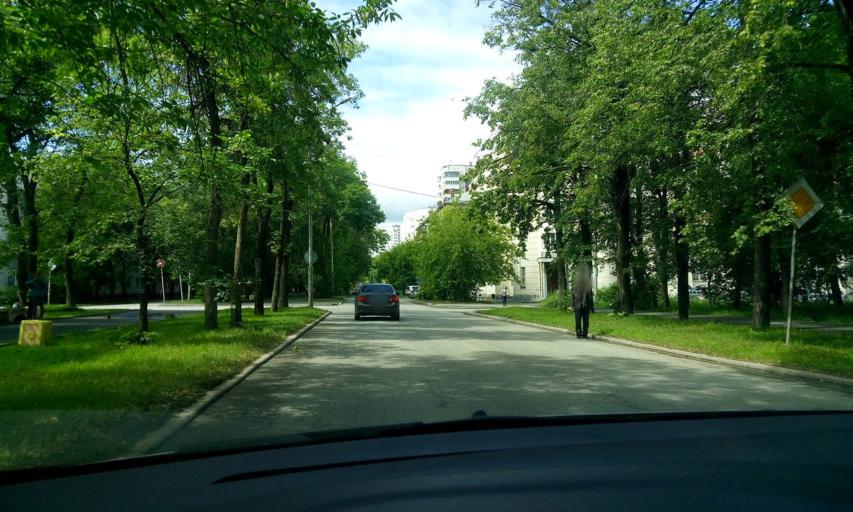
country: RU
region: Sverdlovsk
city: Yekaterinburg
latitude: 56.8891
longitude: 60.6010
